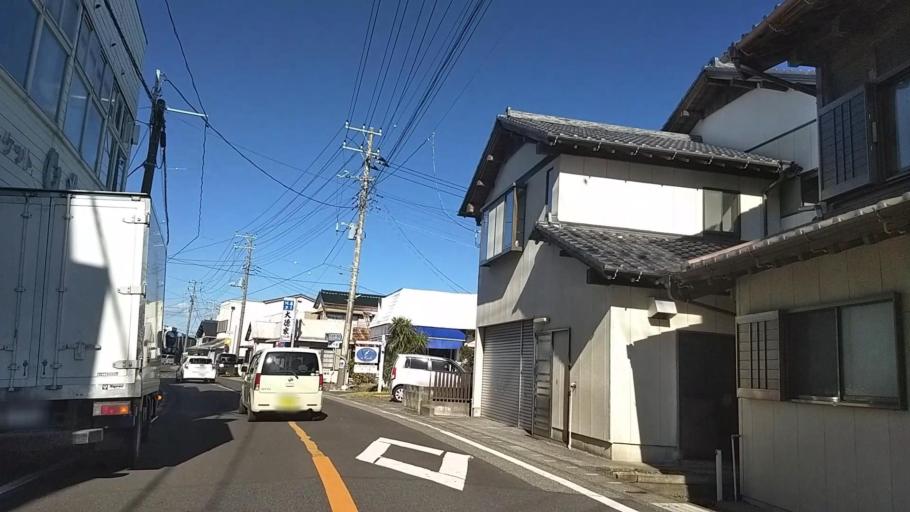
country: JP
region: Chiba
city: Tateyama
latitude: 34.9600
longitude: 139.9591
